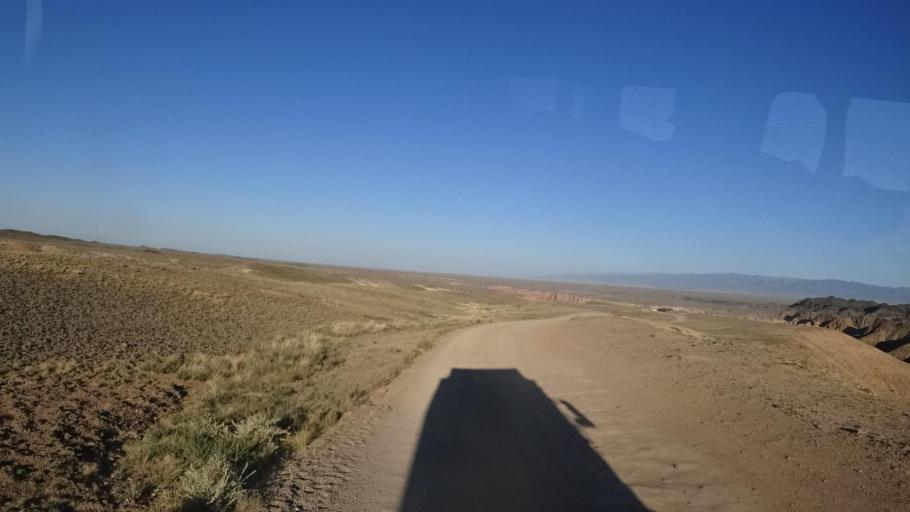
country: KZ
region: Almaty Oblysy
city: Kegen
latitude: 43.3558
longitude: 79.0560
